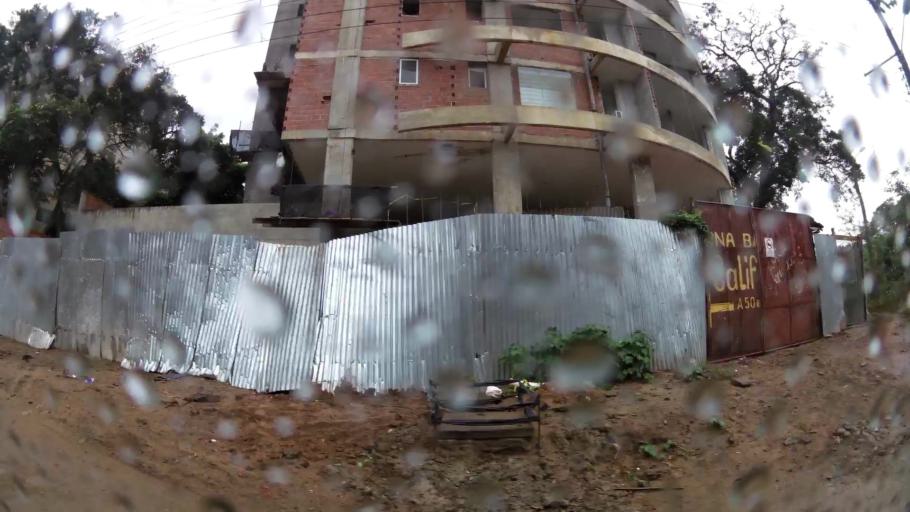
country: BO
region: Santa Cruz
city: Santa Cruz de la Sierra
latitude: -17.7926
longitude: -63.2243
